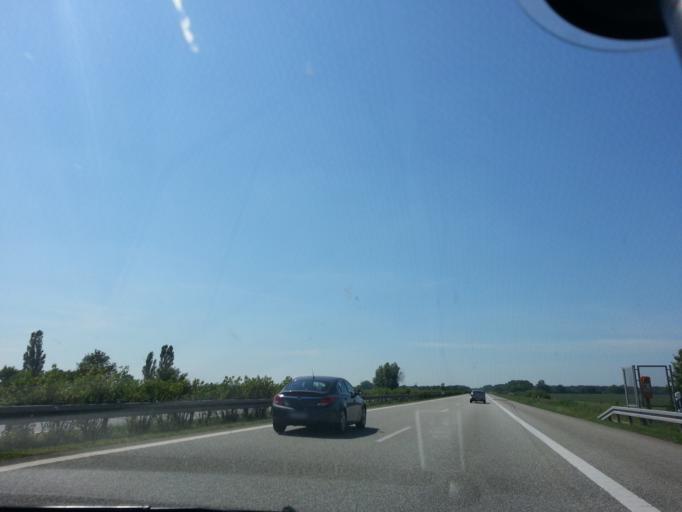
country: DE
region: Mecklenburg-Vorpommern
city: Hagenow
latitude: 53.4896
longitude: 11.1740
